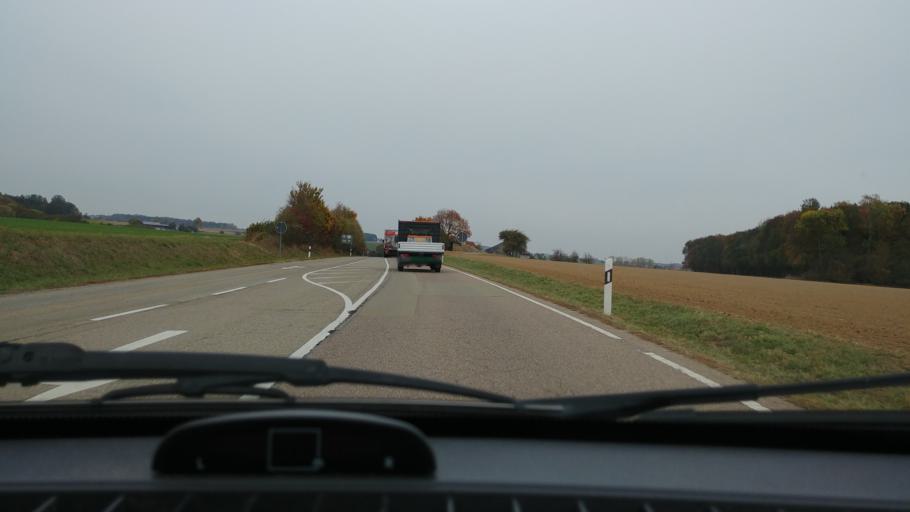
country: DE
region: Baden-Wuerttemberg
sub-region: Regierungsbezirk Stuttgart
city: Rot am See
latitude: 49.2559
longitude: 10.0442
